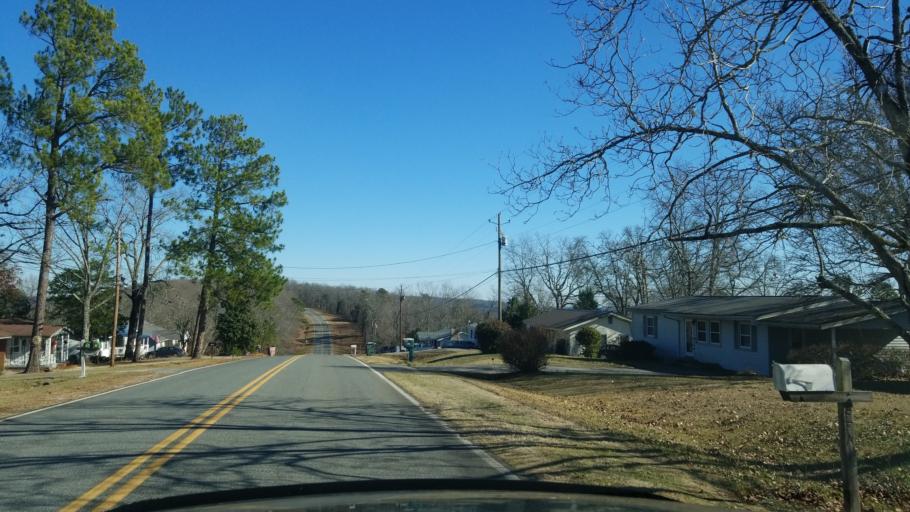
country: US
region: Georgia
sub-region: Meriwether County
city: Manchester
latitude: 32.8437
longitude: -84.6327
